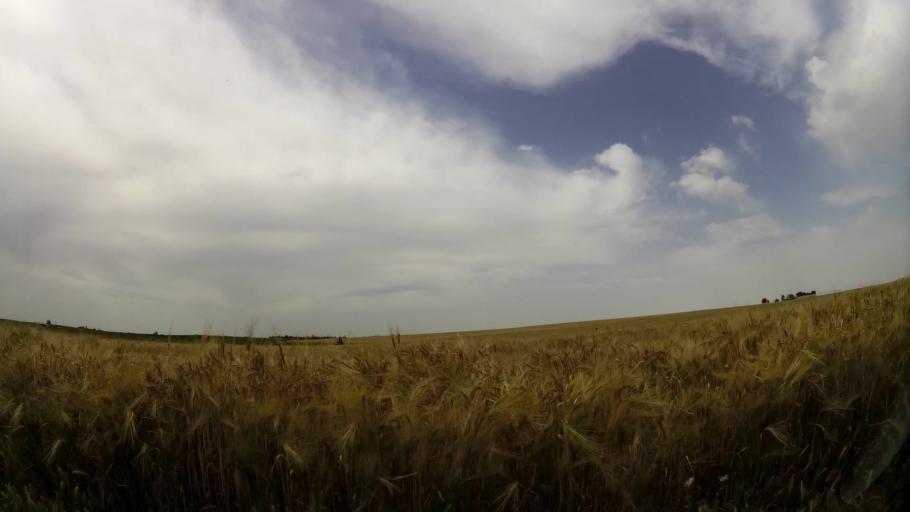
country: MA
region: Rabat-Sale-Zemmour-Zaer
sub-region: Khemisset
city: Tiflet
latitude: 33.7578
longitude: -6.2213
